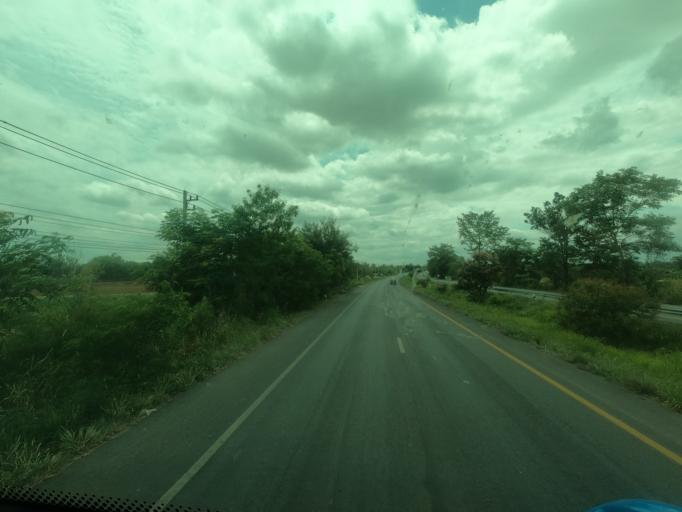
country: TH
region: Nakhon Ratchasima
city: Sung Noen
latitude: 14.8167
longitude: 101.8384
